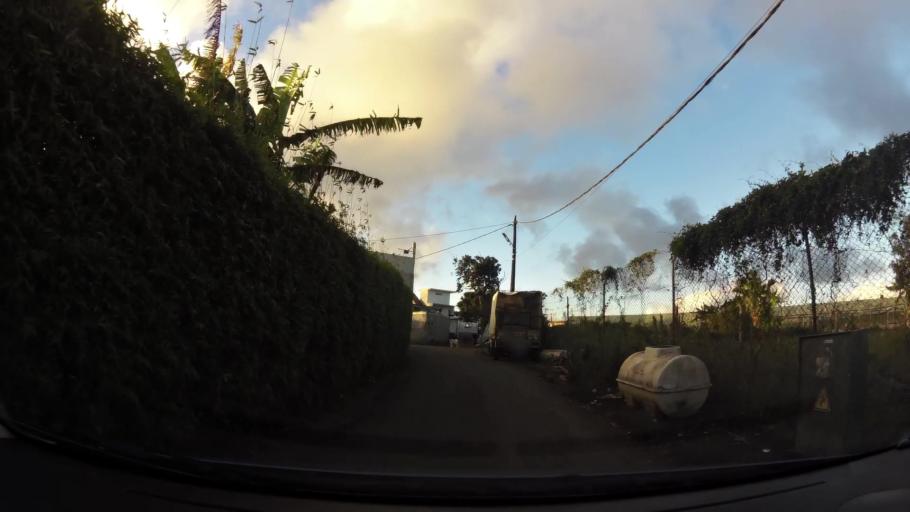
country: MU
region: Plaines Wilhems
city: Curepipe
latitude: -20.3074
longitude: 57.5323
